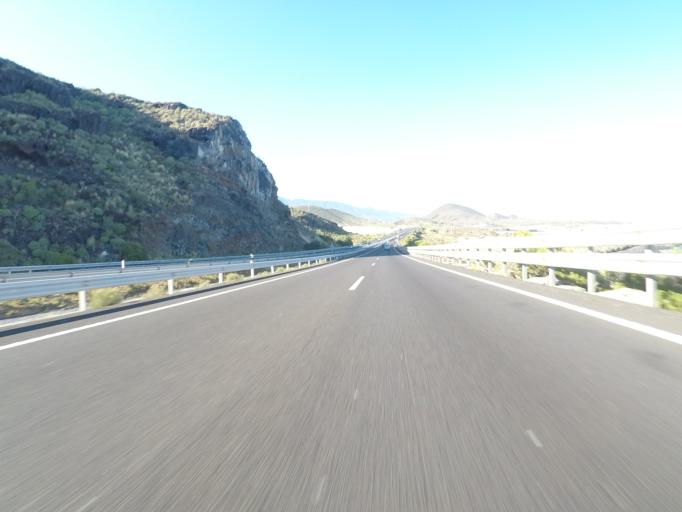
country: ES
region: Canary Islands
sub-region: Provincia de Santa Cruz de Tenerife
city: Guimar
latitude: 28.2835
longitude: -16.3847
